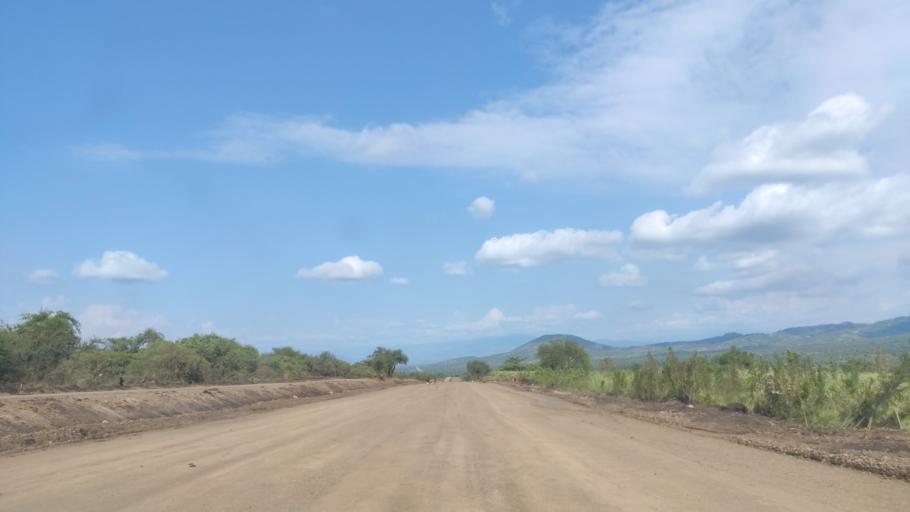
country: ET
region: Southern Nations, Nationalities, and People's Region
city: Felege Neway
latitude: 6.3982
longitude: 37.1154
